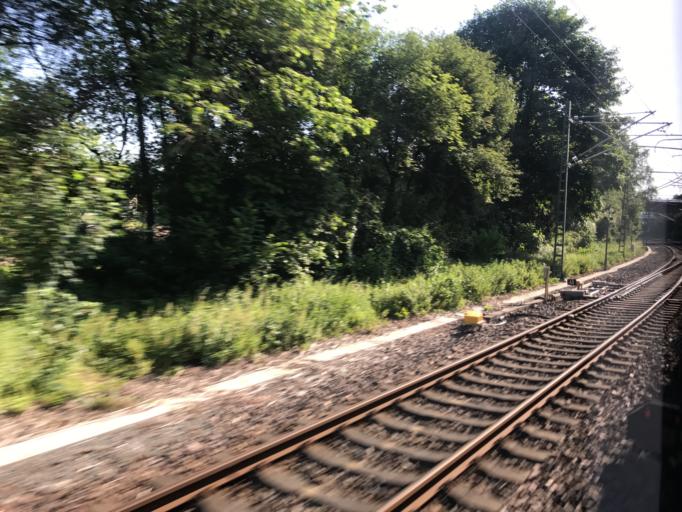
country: DE
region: Rheinland-Pfalz
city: Ellweiler
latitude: 49.6023
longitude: 7.1637
